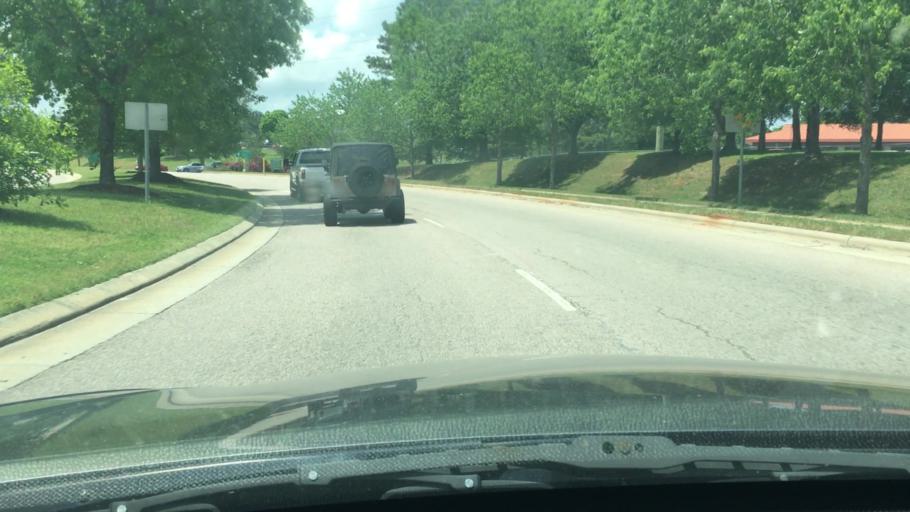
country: US
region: North Carolina
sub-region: Wake County
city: Raleigh
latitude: 35.7612
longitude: -78.6618
